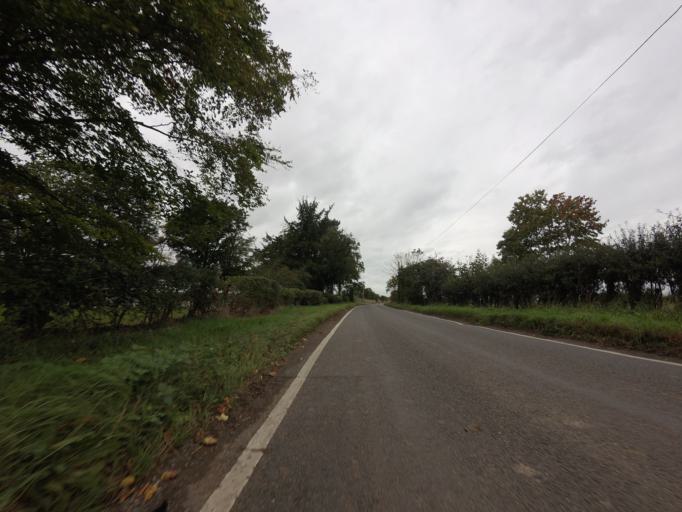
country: GB
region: England
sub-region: Cambridgeshire
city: Harston
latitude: 52.0990
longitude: 0.0619
